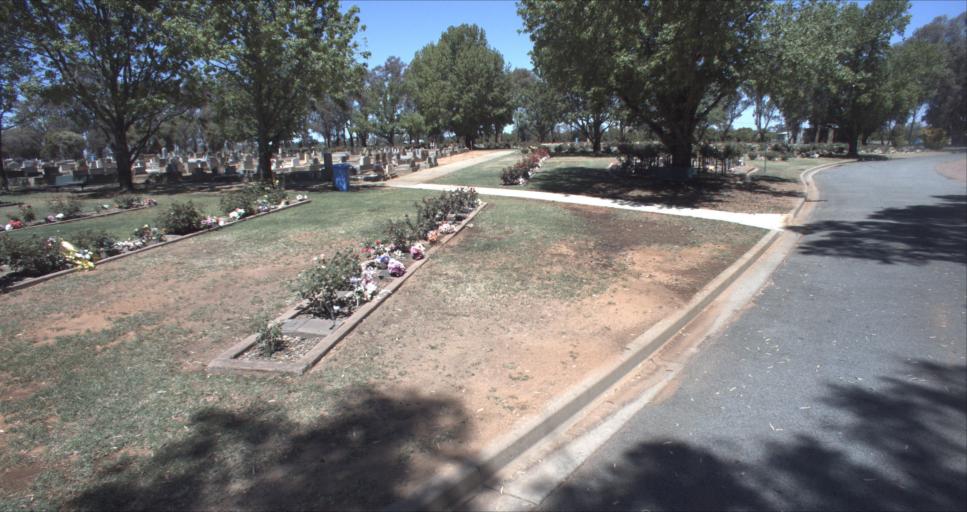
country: AU
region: New South Wales
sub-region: Leeton
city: Leeton
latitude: -34.5317
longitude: 146.3973
